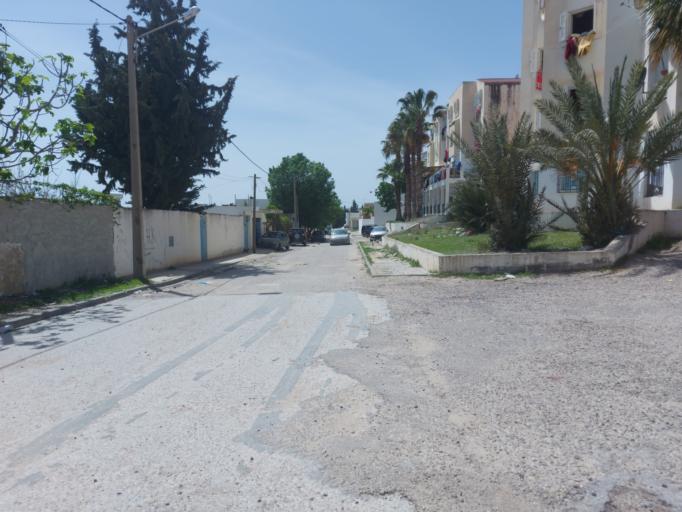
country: TN
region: Kef
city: El Kef
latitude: 36.1818
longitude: 8.7286
